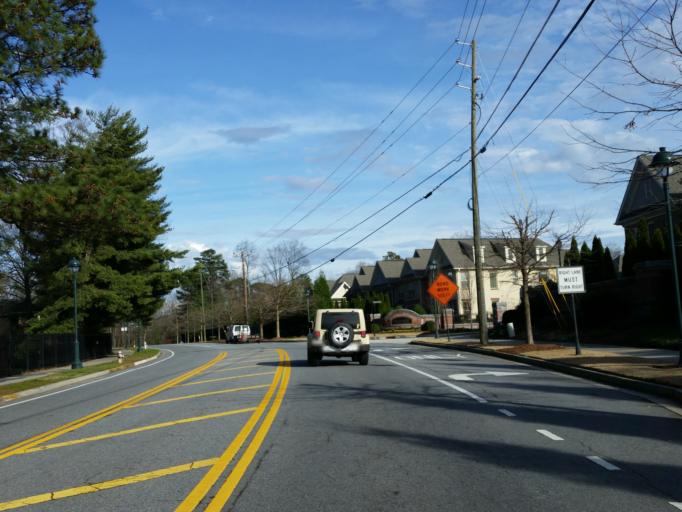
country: US
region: Georgia
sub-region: DeKalb County
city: Dunwoody
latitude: 33.9550
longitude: -84.3620
